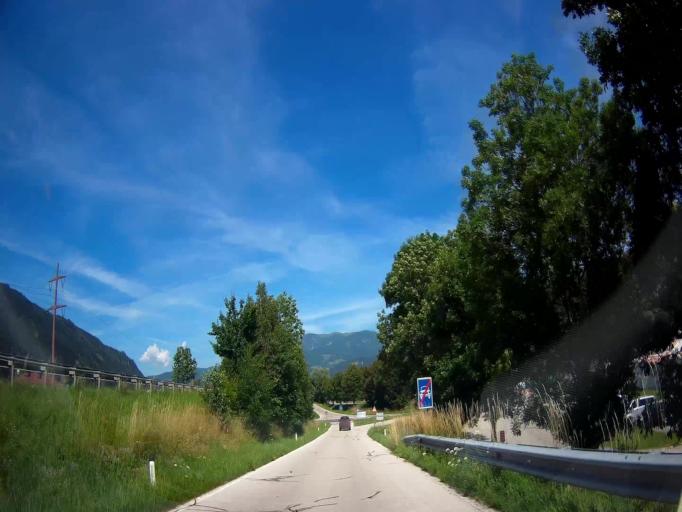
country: AT
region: Carinthia
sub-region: Politischer Bezirk Sankt Veit an der Glan
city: Friesach
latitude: 46.9515
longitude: 14.4209
